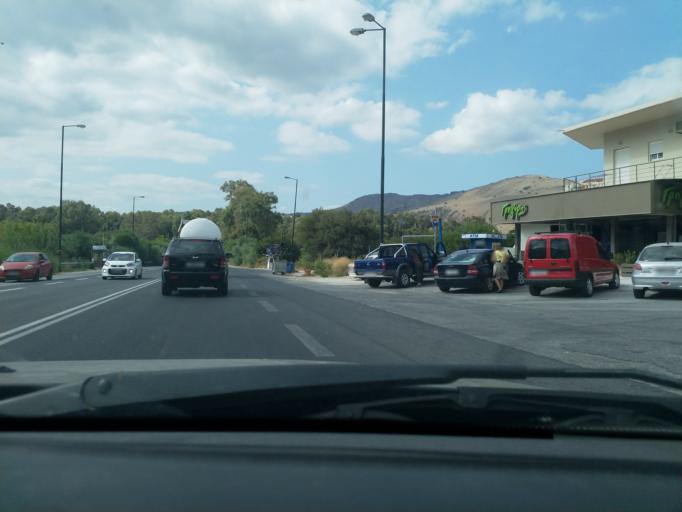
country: GR
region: Crete
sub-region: Nomos Chanias
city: Georgioupolis
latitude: 35.3600
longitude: 24.2591
